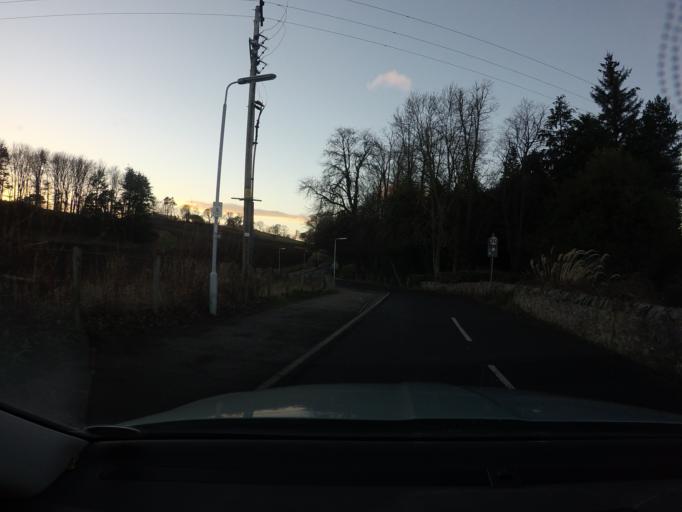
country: GB
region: Scotland
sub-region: Fife
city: Newport-On-Tay
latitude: 56.4327
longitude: -2.9372
